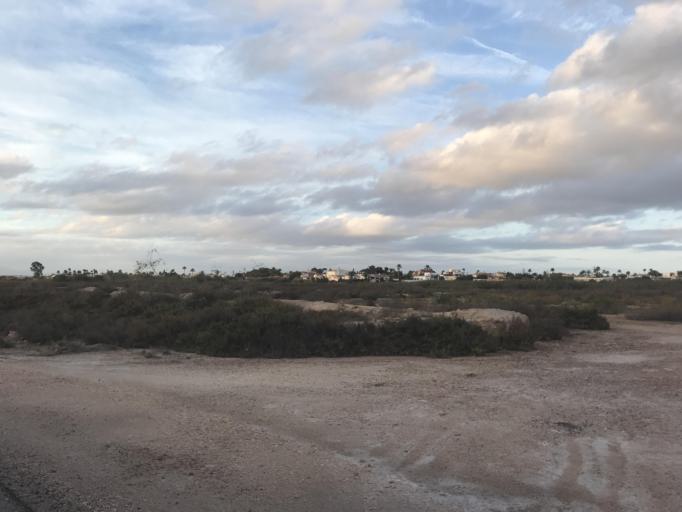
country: ES
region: Valencia
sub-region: Provincia de Alicante
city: Torrevieja
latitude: 37.9805
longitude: -0.6991
